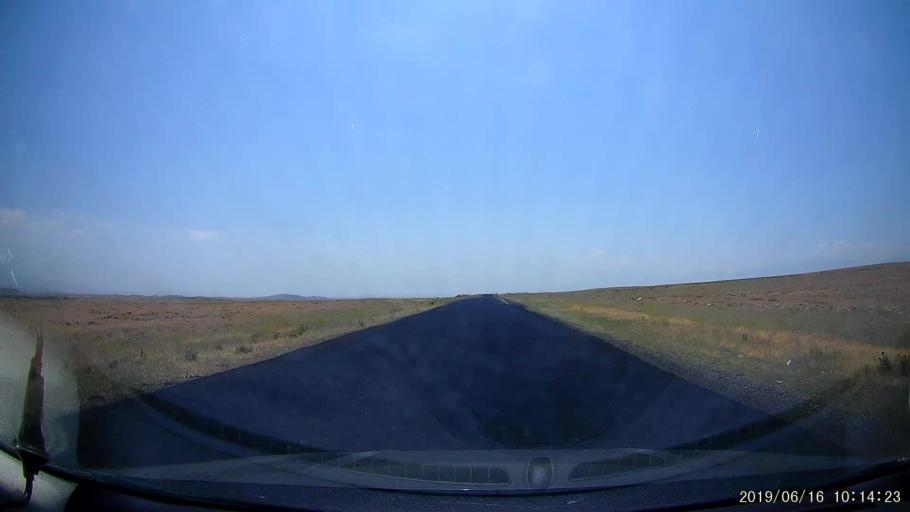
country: TR
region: Igdir
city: Tuzluca
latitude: 40.1853
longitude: 43.6616
